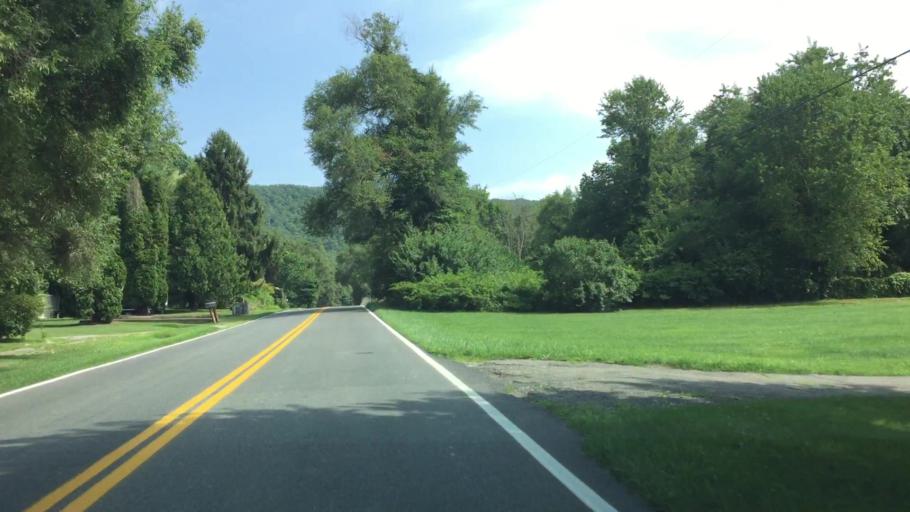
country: US
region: Virginia
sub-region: Pulaski County
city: Pulaski
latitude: 37.0007
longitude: -80.7997
